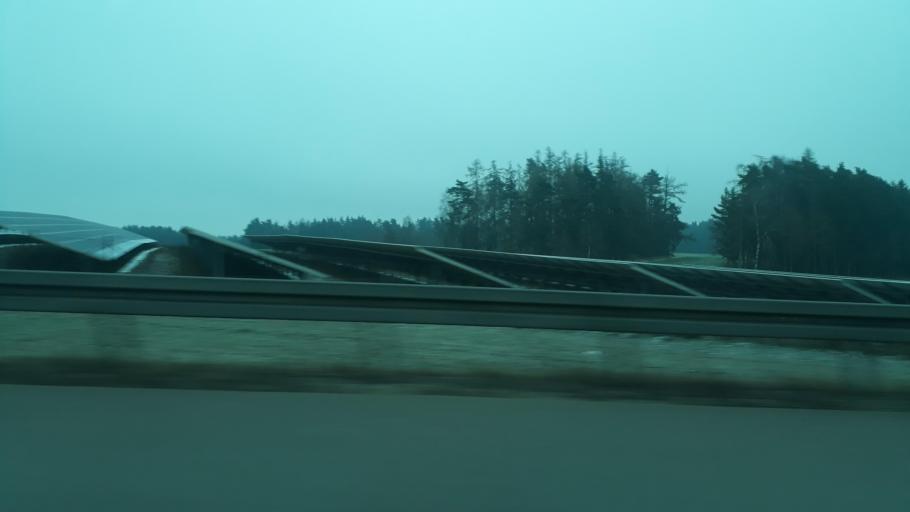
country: DE
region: Bavaria
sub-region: Upper Palatinate
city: Stulln
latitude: 49.4605
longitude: 12.1334
